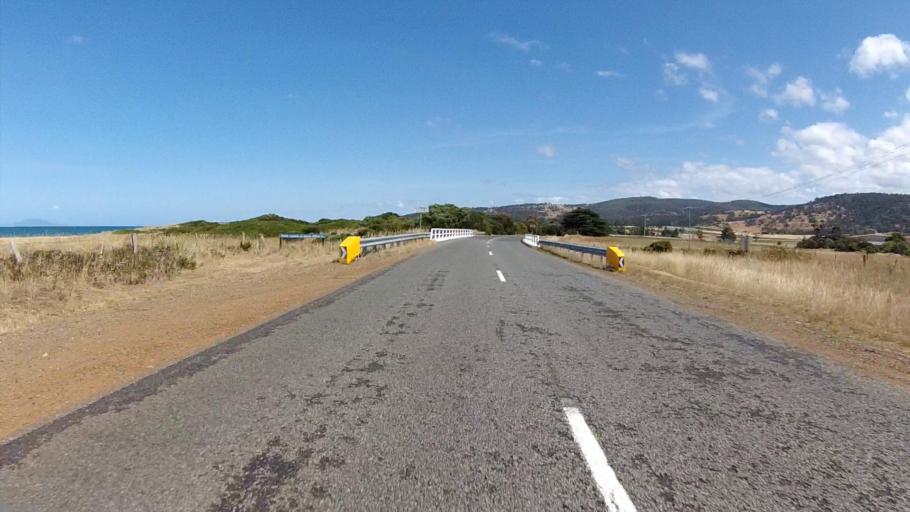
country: AU
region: Tasmania
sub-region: Sorell
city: Sorell
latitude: -42.1978
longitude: 148.0501
